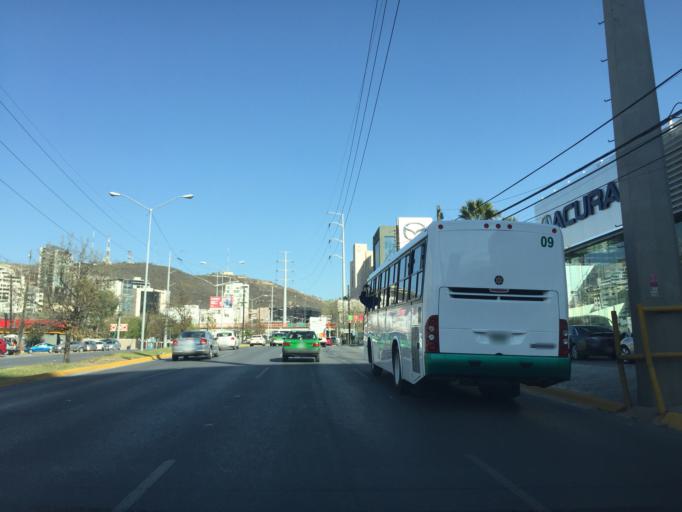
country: MX
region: Nuevo Leon
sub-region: Monterrey
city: Monterrey
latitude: 25.6535
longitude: -100.3431
